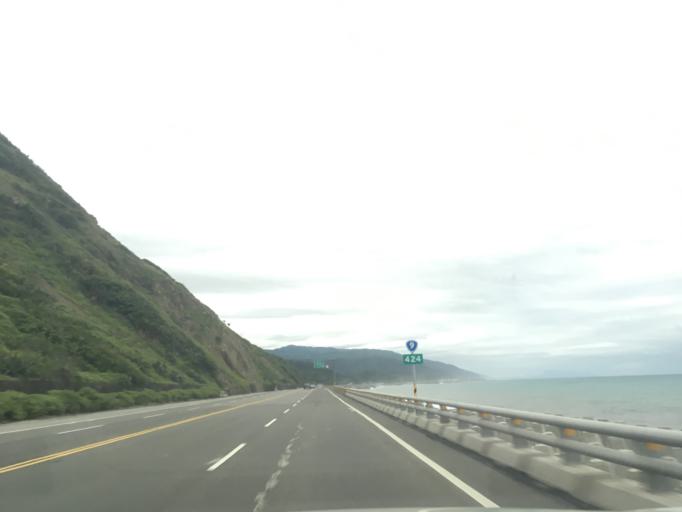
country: TW
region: Taiwan
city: Hengchun
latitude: 22.3133
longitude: 120.8913
